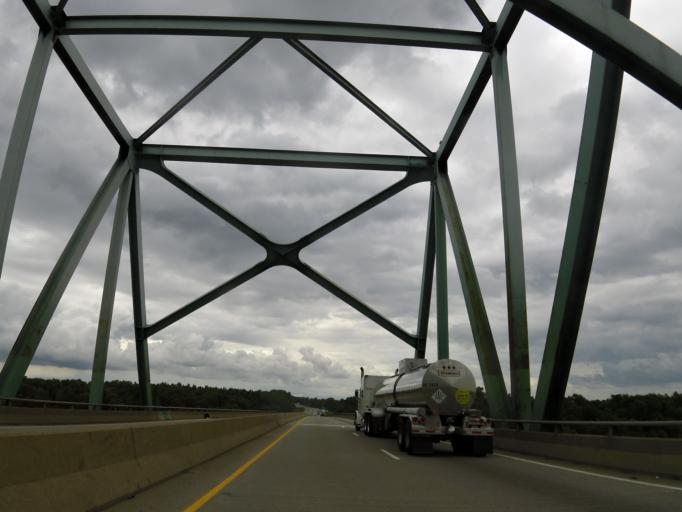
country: US
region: Illinois
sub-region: Alexander County
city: Cairo
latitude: 37.0247
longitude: -89.2106
